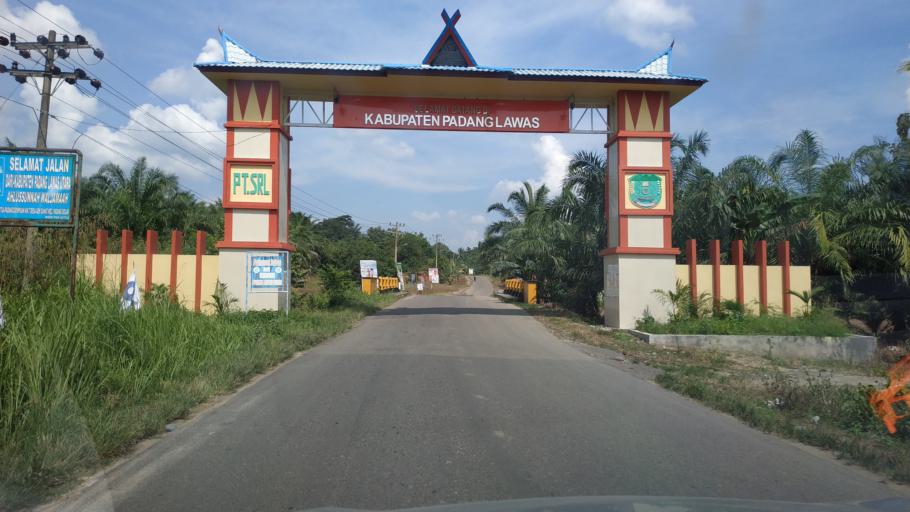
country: ID
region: North Sumatra
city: Binanga
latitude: 1.4143
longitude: 99.7368
